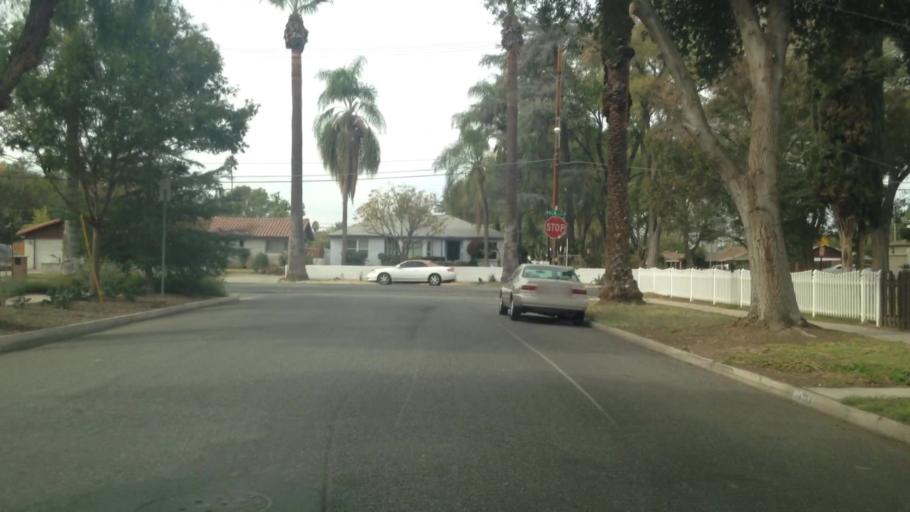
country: US
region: California
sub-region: Riverside County
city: Riverside
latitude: 33.9597
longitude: -117.4006
